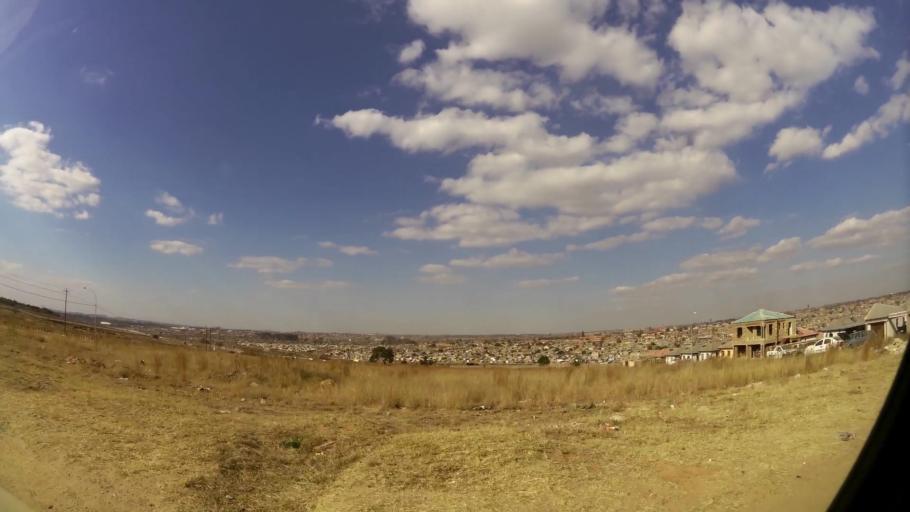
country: ZA
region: Gauteng
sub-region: Ekurhuleni Metropolitan Municipality
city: Tembisa
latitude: -25.9784
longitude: 28.1907
